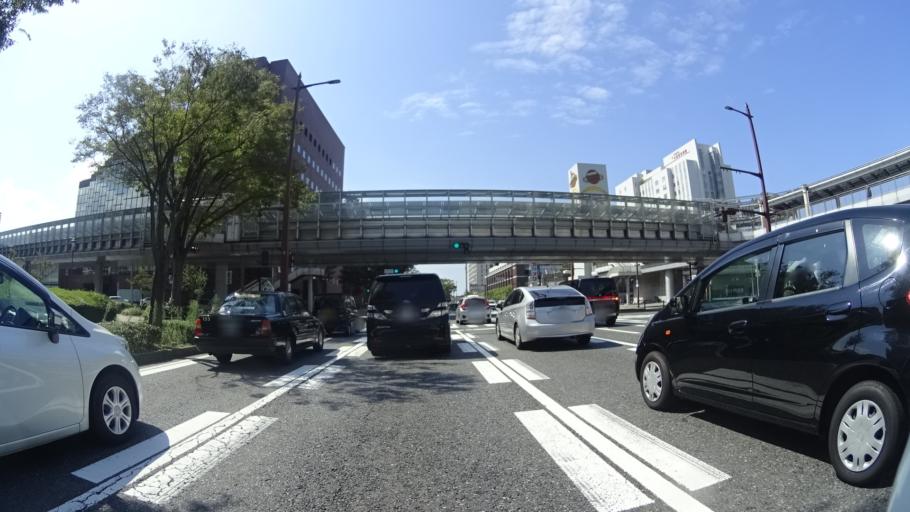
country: JP
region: Fukuoka
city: Kitakyushu
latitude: 33.8891
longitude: 130.8846
